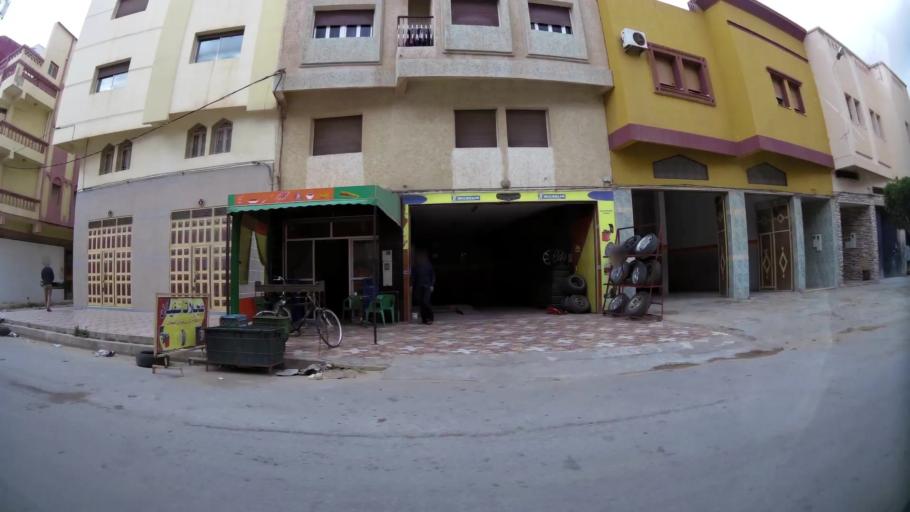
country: MA
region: Oriental
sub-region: Nador
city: Nador
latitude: 35.1595
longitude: -2.9338
